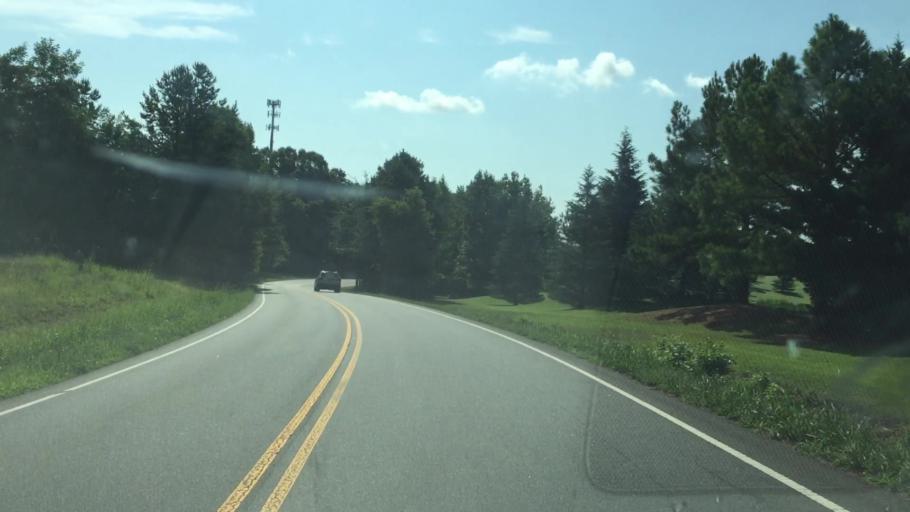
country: US
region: North Carolina
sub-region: Mecklenburg County
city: Mint Hill
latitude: 35.1699
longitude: -80.6029
